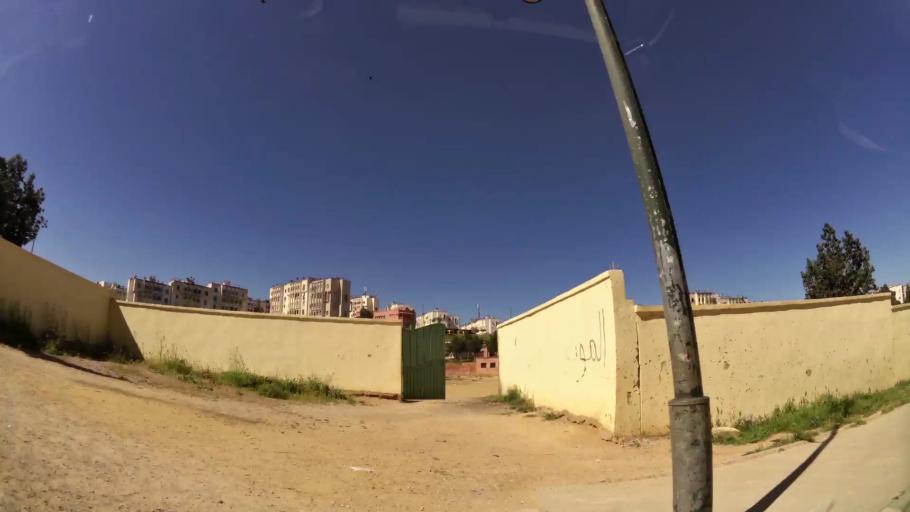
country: MA
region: Meknes-Tafilalet
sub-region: Meknes
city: Meknes
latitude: 33.9078
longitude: -5.5400
